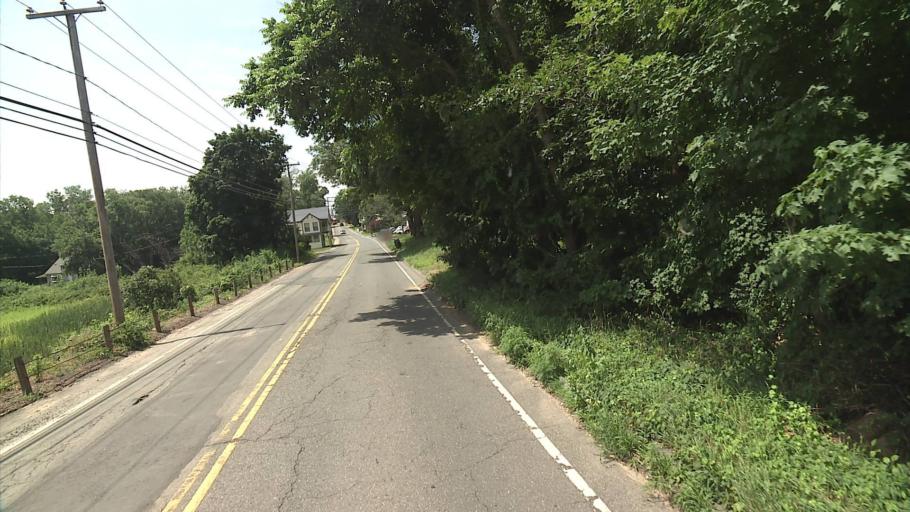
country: US
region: Connecticut
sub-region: Tolland County
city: South Coventry
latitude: 41.7663
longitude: -72.2926
